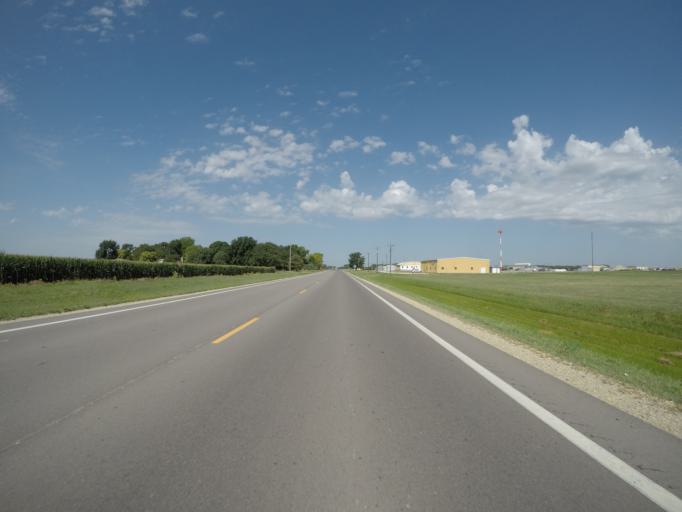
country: US
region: Kansas
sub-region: Clay County
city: Clay Center
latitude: 39.3801
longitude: -97.1610
